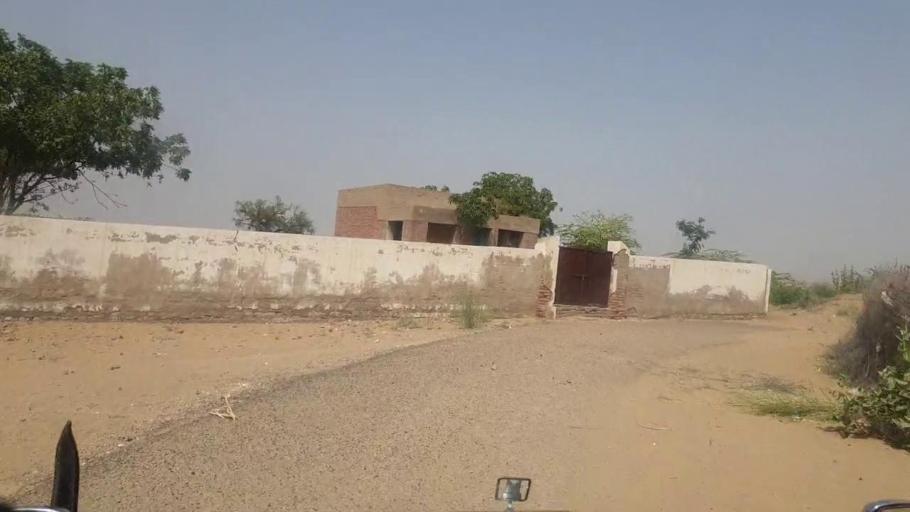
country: PK
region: Sindh
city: Islamkot
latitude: 25.1570
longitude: 70.2010
